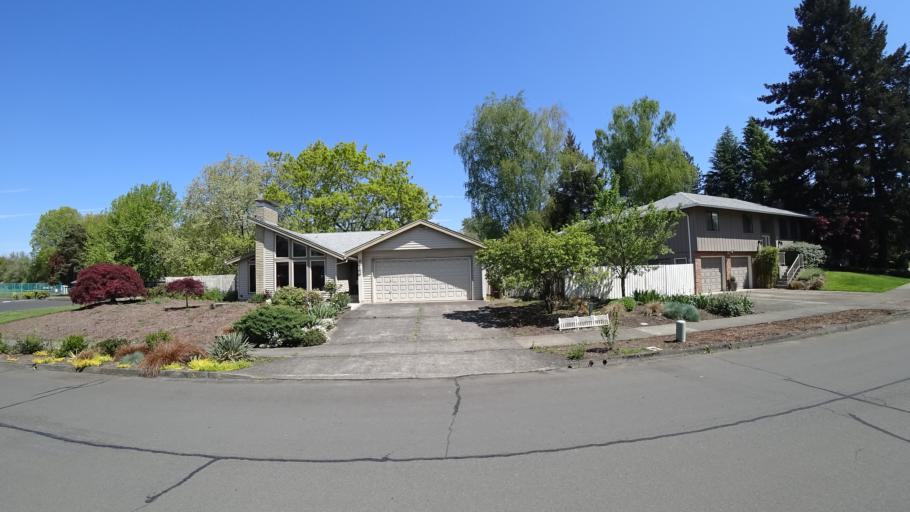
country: US
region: Oregon
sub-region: Washington County
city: Hillsboro
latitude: 45.4994
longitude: -122.9599
